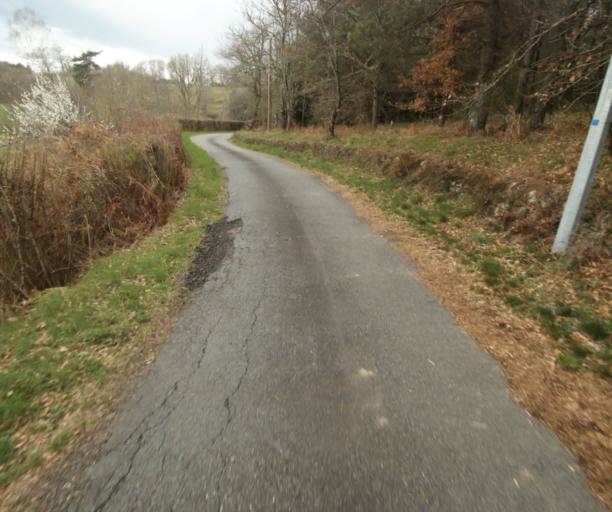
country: FR
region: Limousin
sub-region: Departement de la Correze
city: Correze
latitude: 45.3130
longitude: 1.8911
